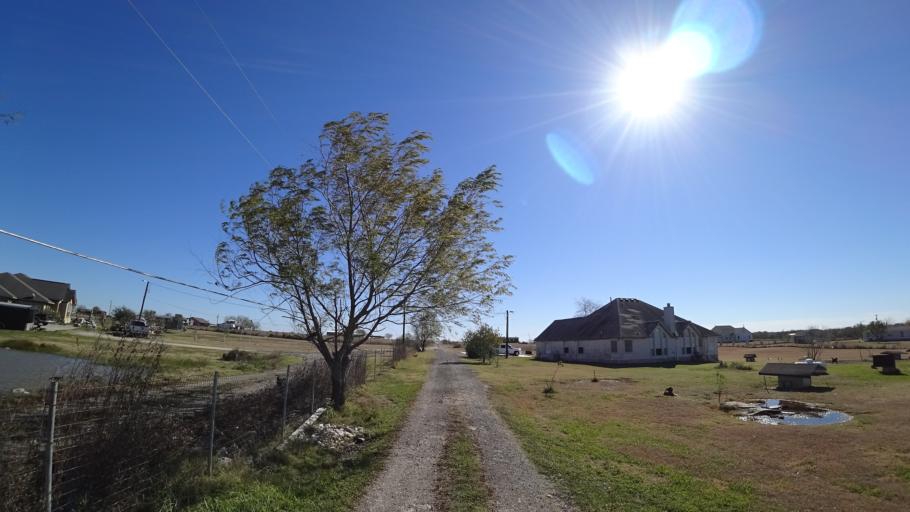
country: US
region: Texas
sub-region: Travis County
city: Garfield
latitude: 30.0999
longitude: -97.6200
